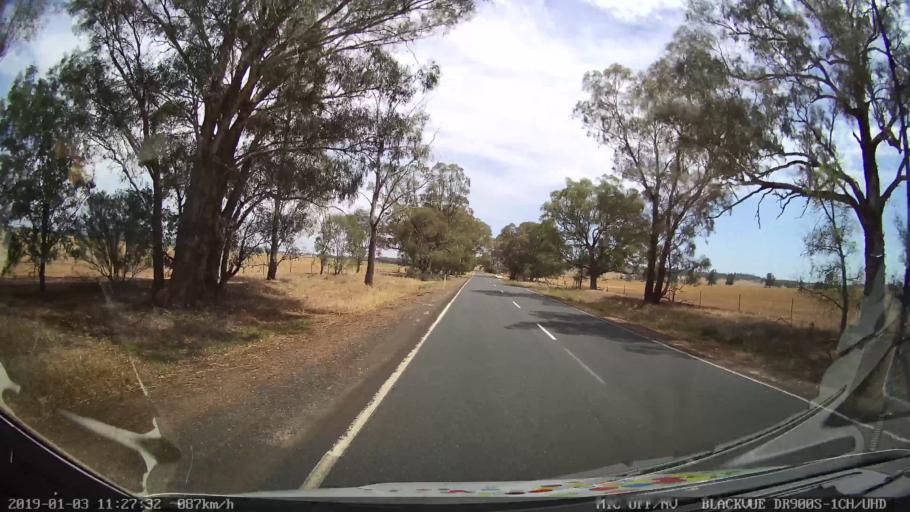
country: AU
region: New South Wales
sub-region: Weddin
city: Grenfell
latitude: -34.0115
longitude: 148.2182
